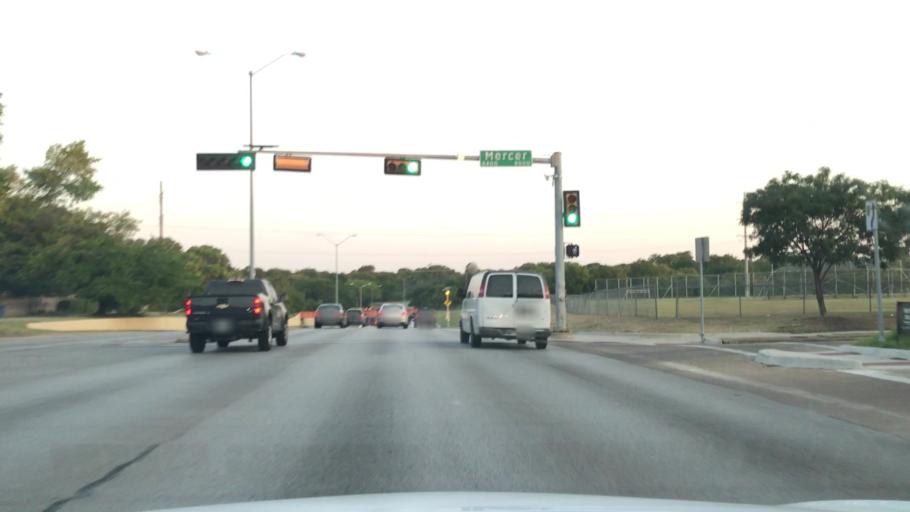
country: US
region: Texas
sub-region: Dallas County
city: Highland Park
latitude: 32.8225
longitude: -96.6939
